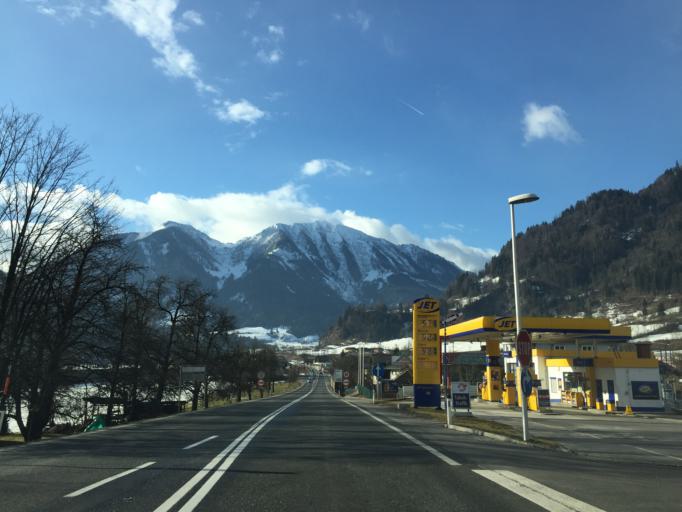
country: AT
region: Salzburg
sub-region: Politischer Bezirk Sankt Johann im Pongau
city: Sankt Johann im Pongau
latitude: 47.3439
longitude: 13.1922
